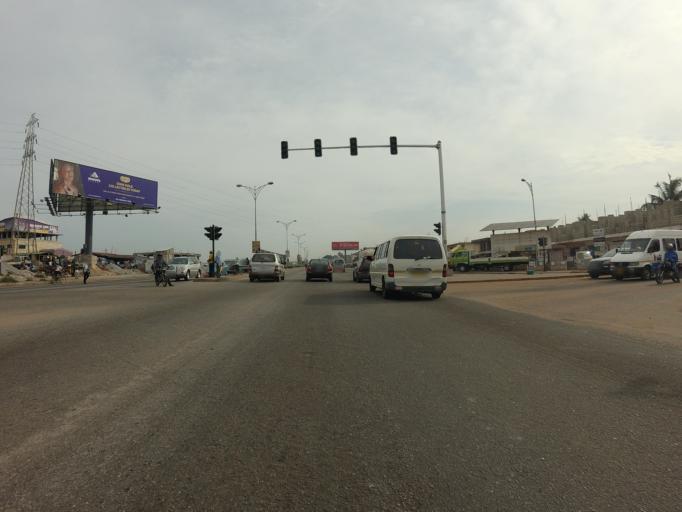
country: GH
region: Greater Accra
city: Gbawe
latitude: 5.5841
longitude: -0.2740
